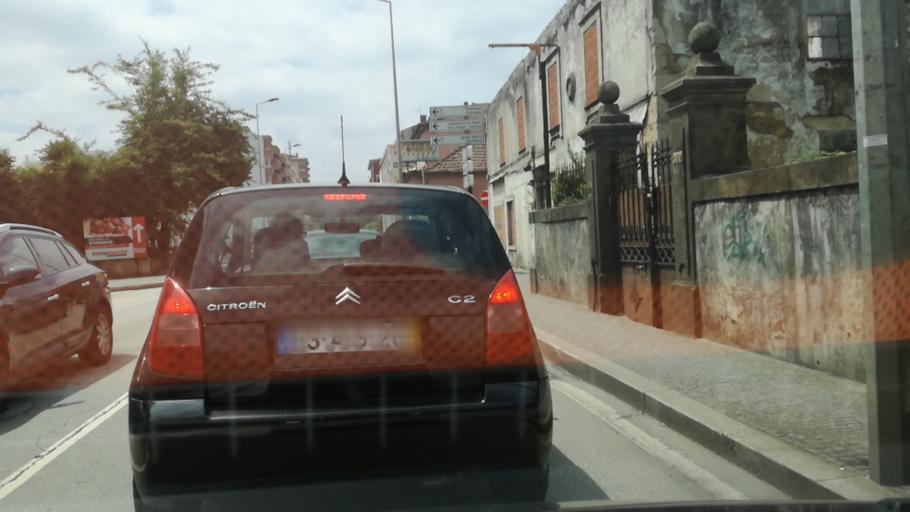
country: PT
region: Porto
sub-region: Trofa
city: Bougado
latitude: 41.3411
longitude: -8.5579
